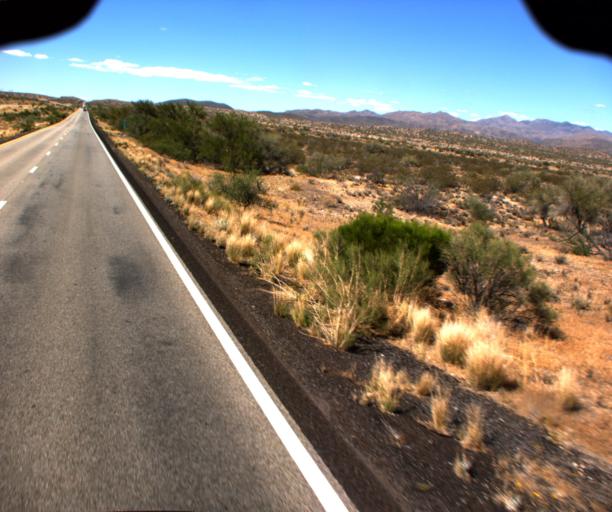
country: US
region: Arizona
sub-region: Mohave County
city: Kingman
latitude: 34.8829
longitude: -113.6487
